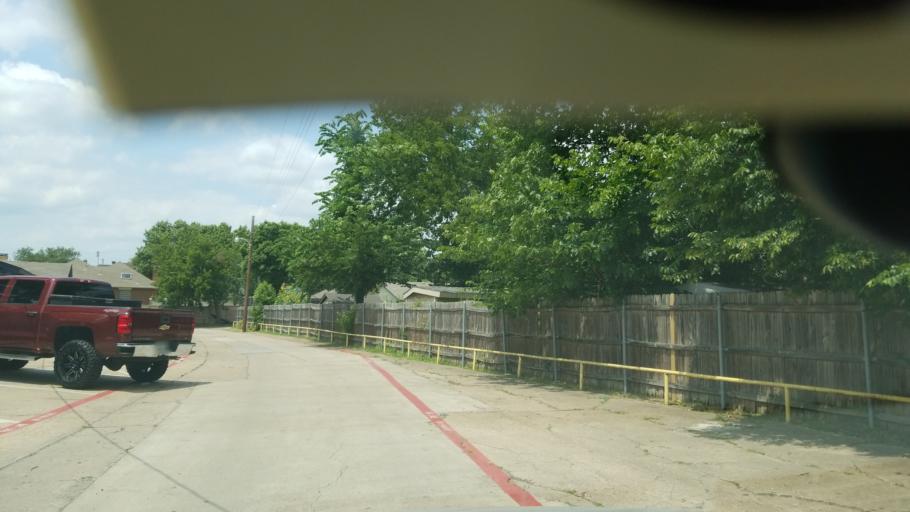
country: US
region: Texas
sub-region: Dallas County
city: Irving
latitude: 32.8480
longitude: -96.9574
